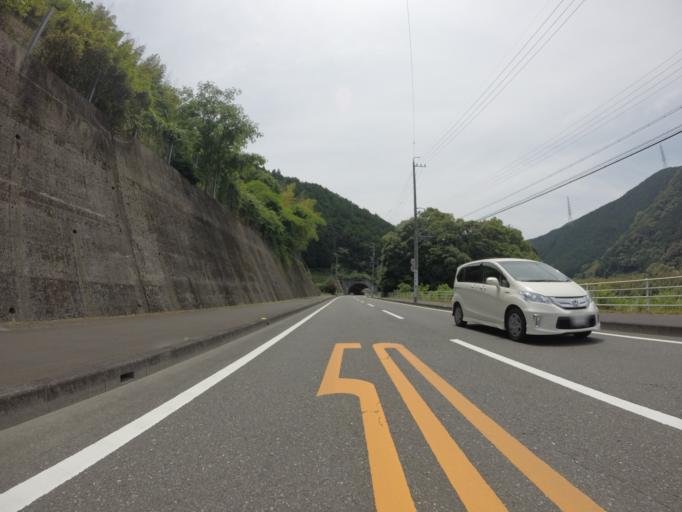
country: JP
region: Shizuoka
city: Shizuoka-shi
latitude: 35.0034
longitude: 138.2863
